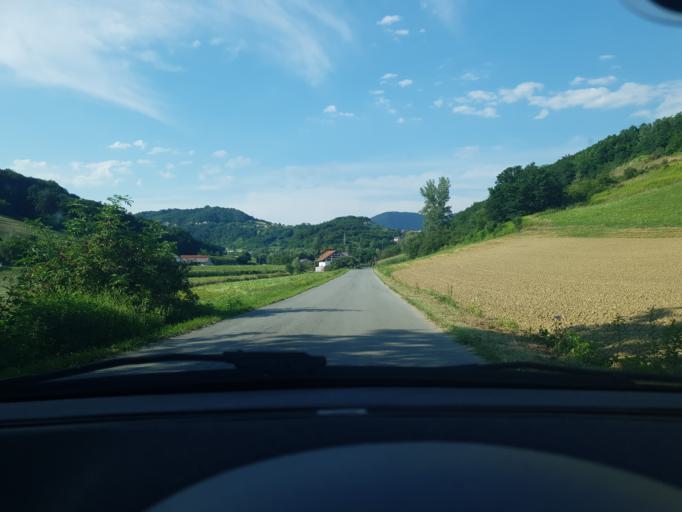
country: HR
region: Krapinsko-Zagorska
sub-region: Grad Krapina
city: Krapina
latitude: 46.1486
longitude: 15.8516
